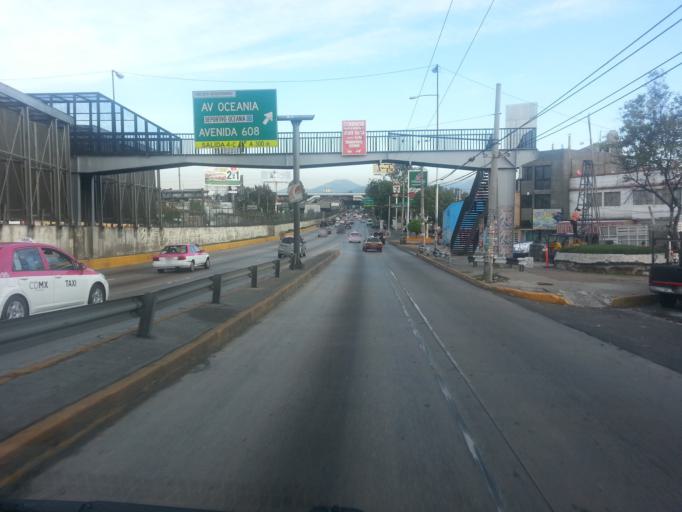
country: MX
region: Mexico City
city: Venustiano Carranza
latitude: 19.4421
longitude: -99.0854
